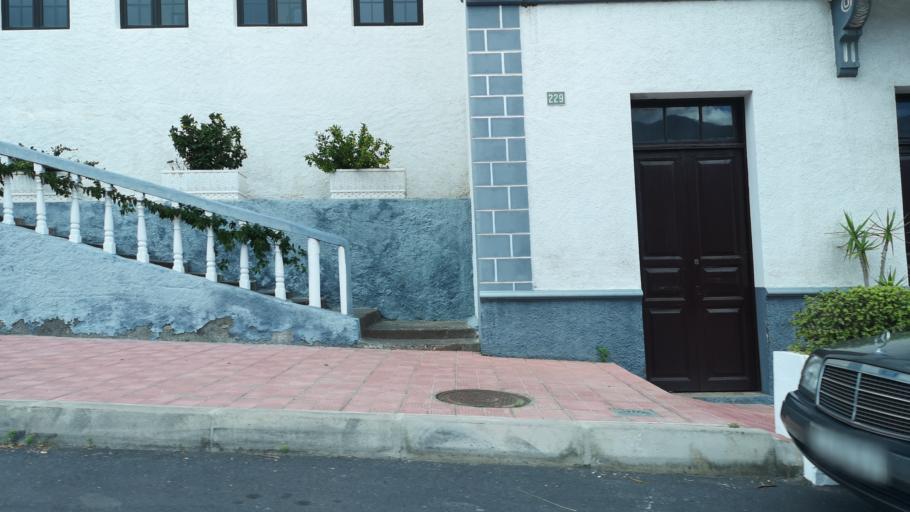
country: ES
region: Canary Islands
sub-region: Provincia de Santa Cruz de Tenerife
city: Hermigua
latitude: 28.1735
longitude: -17.1875
